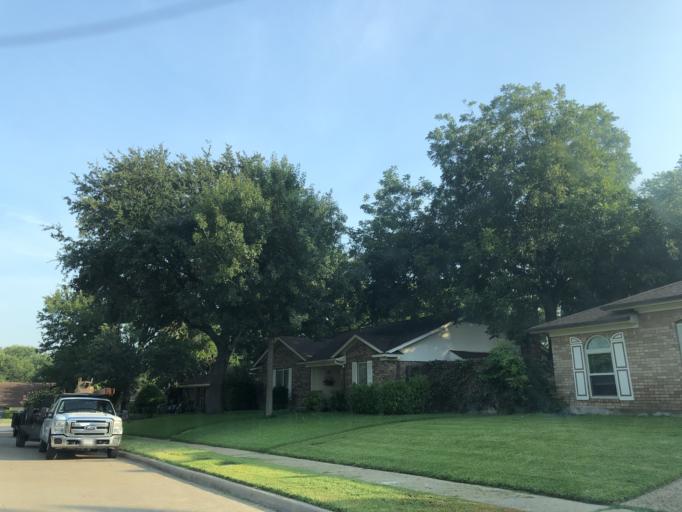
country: US
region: Texas
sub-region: Dallas County
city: Garland
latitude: 32.8667
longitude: -96.6236
